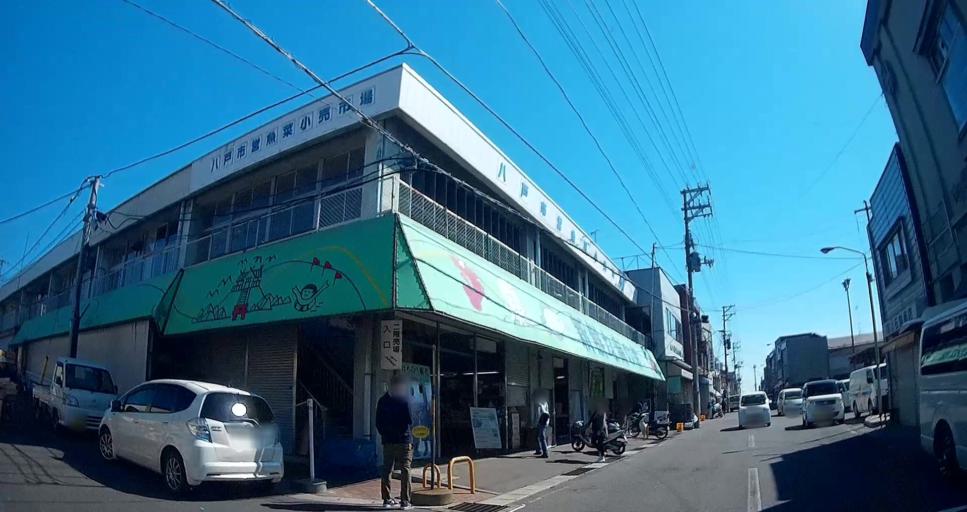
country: JP
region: Aomori
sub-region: Hachinohe Shi
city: Uchimaru
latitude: 40.5234
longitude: 141.5270
